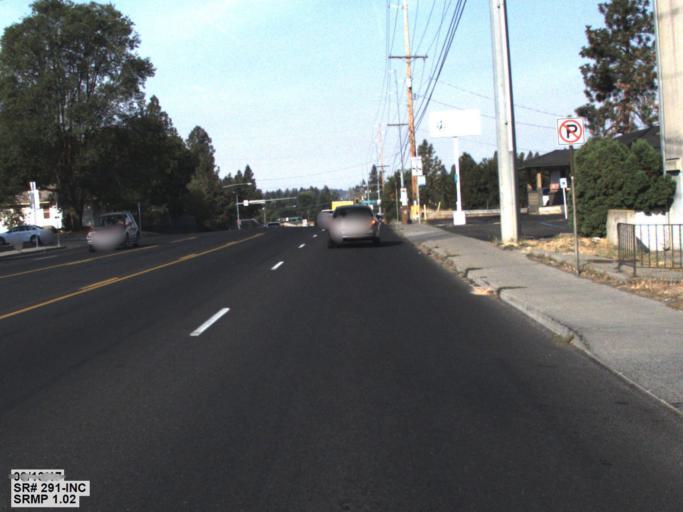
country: US
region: Washington
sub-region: Spokane County
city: Town and Country
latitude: 47.7154
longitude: -117.4330
